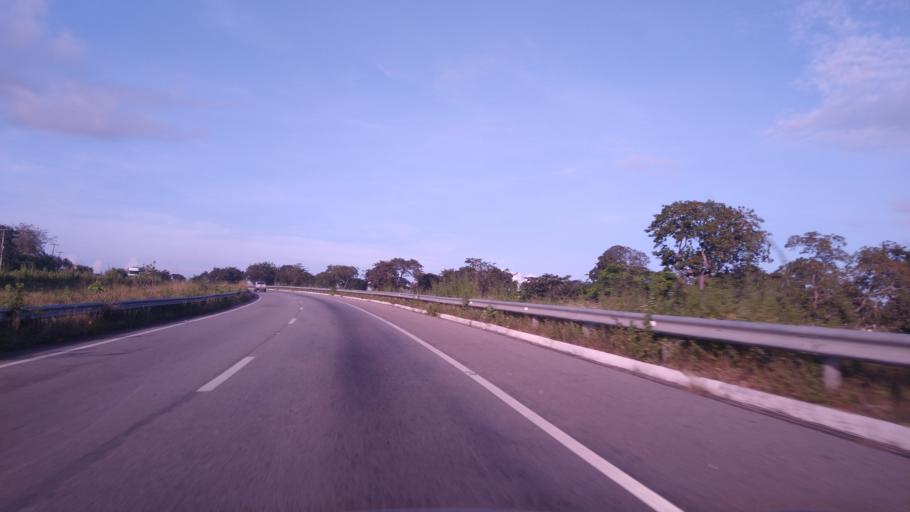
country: BR
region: Ceara
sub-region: Pacajus
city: Pacajus
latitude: -4.1674
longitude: -38.4922
